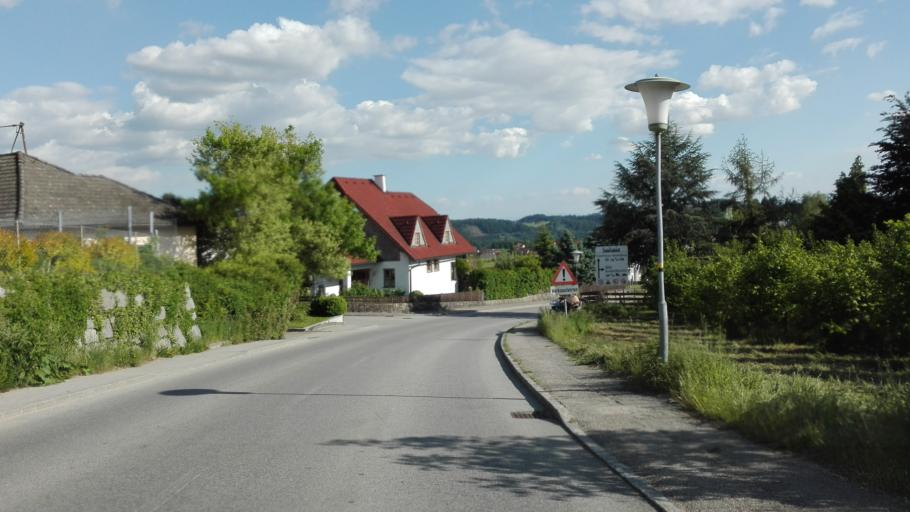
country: AT
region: Upper Austria
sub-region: Politischer Bezirk Perg
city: Perg
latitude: 48.3282
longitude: 14.6232
